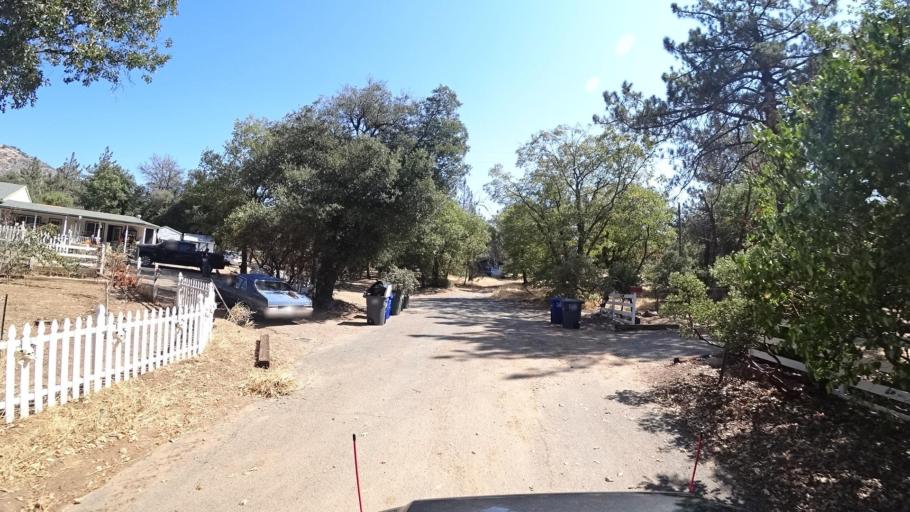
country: US
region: California
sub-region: San Diego County
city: Julian
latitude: 33.0858
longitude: -116.5852
